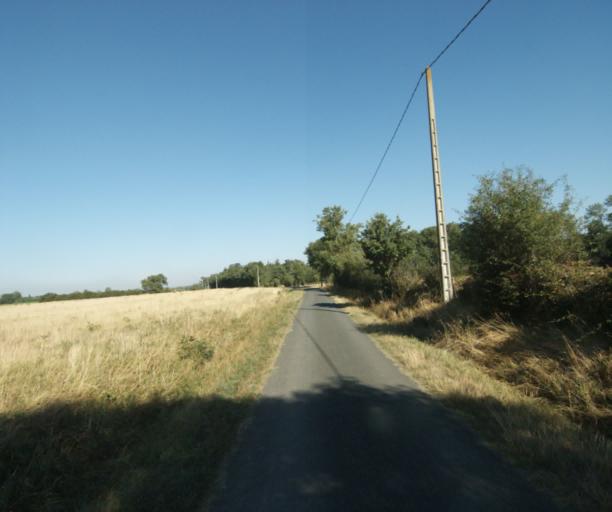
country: FR
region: Midi-Pyrenees
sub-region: Departement de la Haute-Garonne
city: Revel
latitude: 43.4607
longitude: 2.0277
